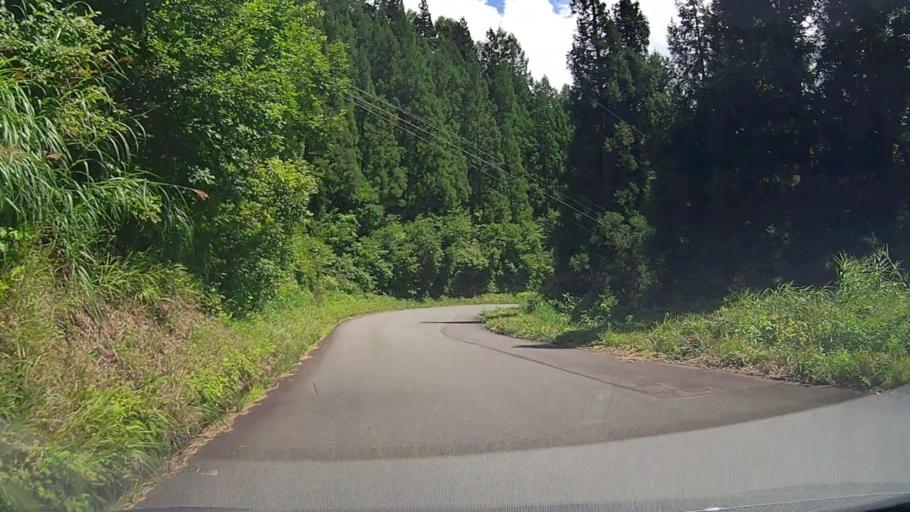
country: JP
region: Nagano
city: Iiyama
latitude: 36.9346
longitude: 138.4609
